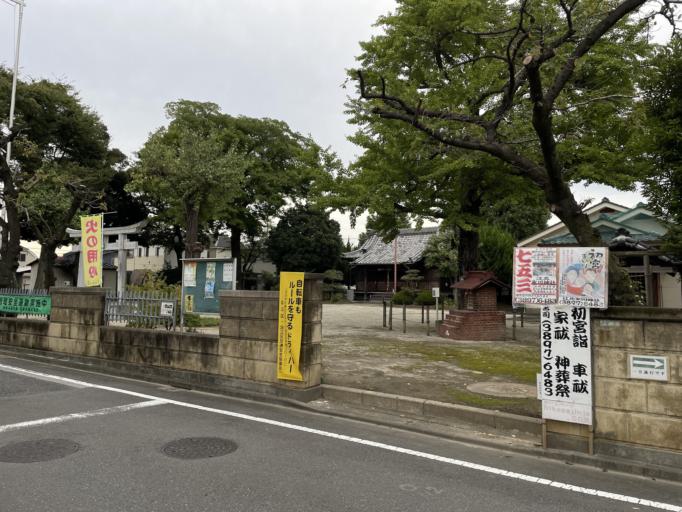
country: JP
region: Saitama
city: Kawaguchi
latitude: 35.7816
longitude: 139.7498
